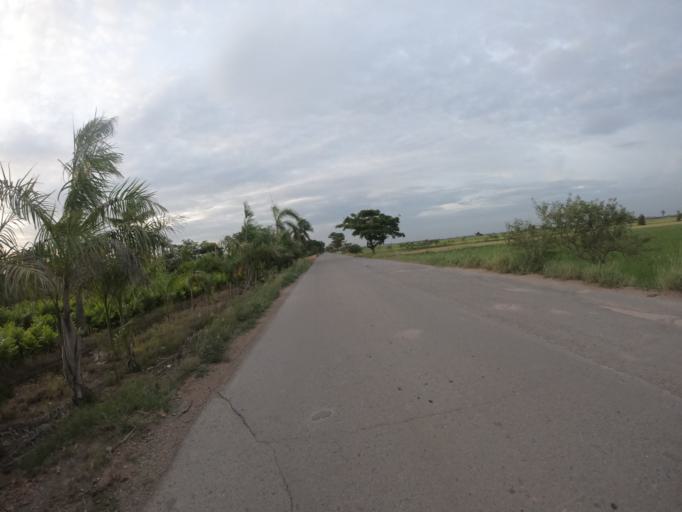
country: TH
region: Pathum Thani
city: Ban Lam Luk Ka
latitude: 13.9971
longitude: 100.7999
